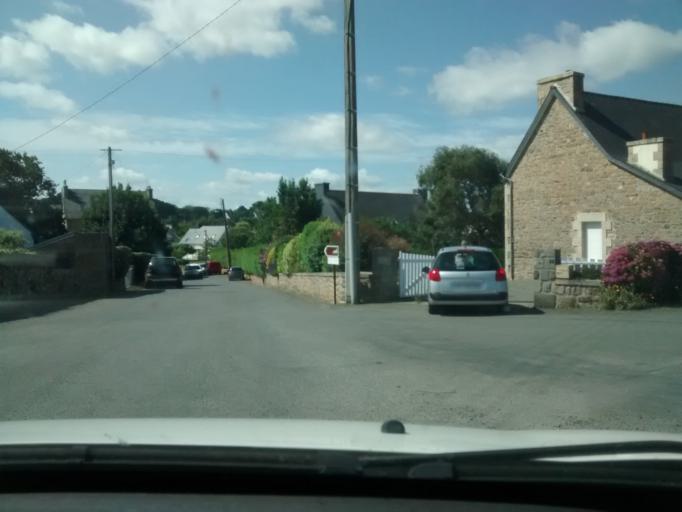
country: FR
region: Brittany
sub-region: Departement des Cotes-d'Armor
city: Trevou-Treguignec
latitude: 48.8330
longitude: -3.3215
